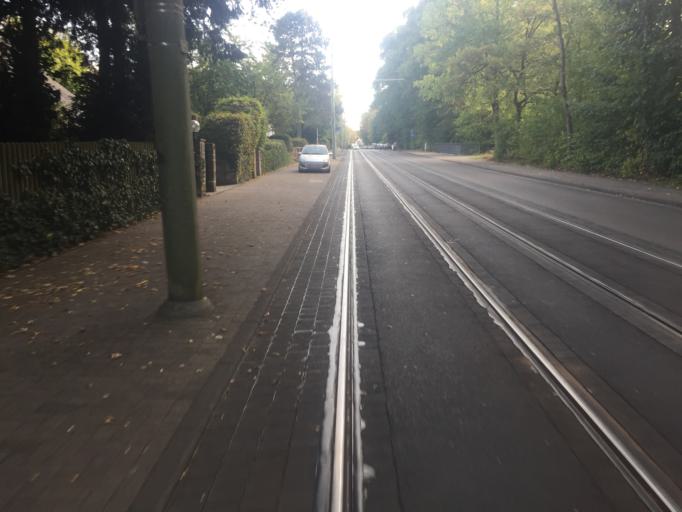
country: DE
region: Hesse
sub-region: Regierungsbezirk Kassel
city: Baunatal
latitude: 51.3062
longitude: 9.4162
